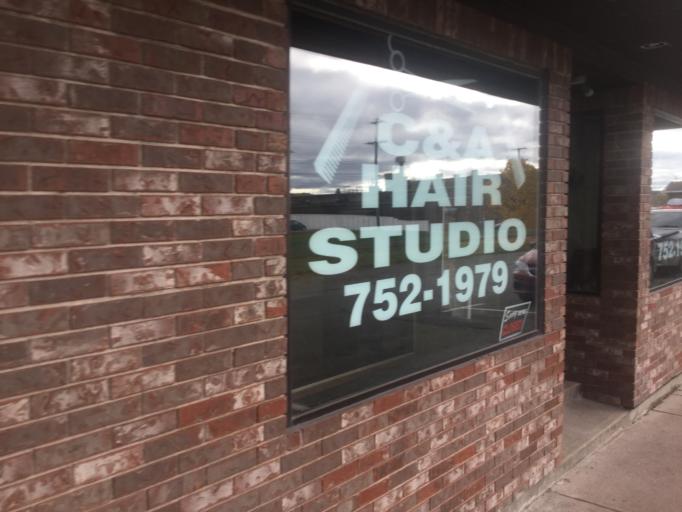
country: CA
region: Nova Scotia
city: New Glasgow
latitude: 45.5851
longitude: -62.6462
